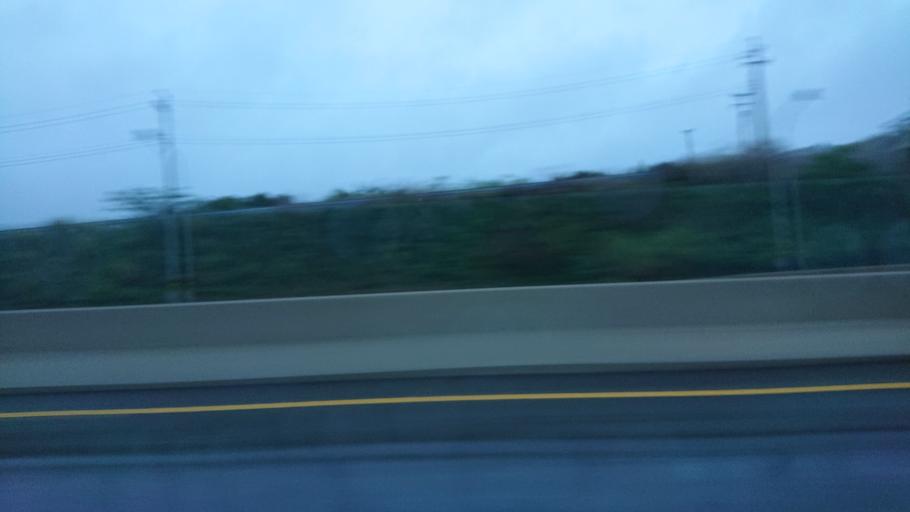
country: TW
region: Taiwan
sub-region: Miaoli
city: Miaoli
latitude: 24.5448
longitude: 120.7024
